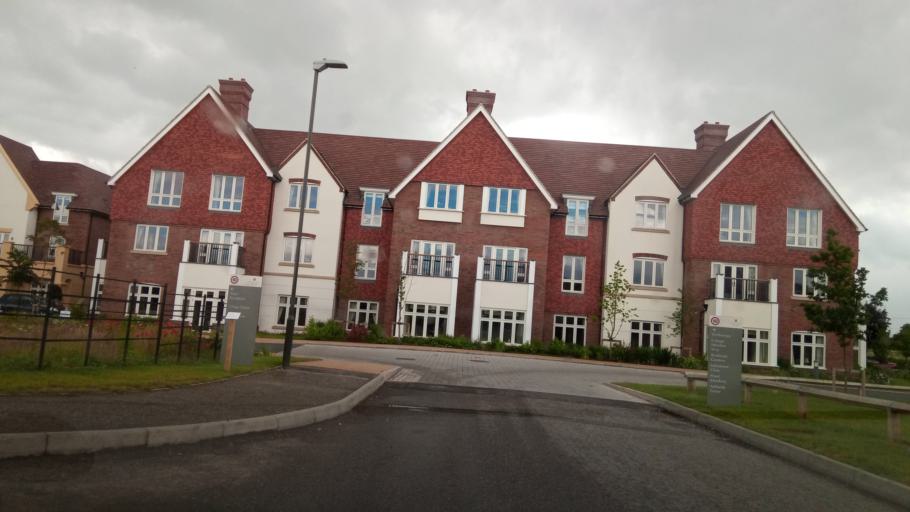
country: GB
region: England
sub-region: Leicestershire
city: Castle Donington
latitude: 52.8558
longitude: -1.3878
